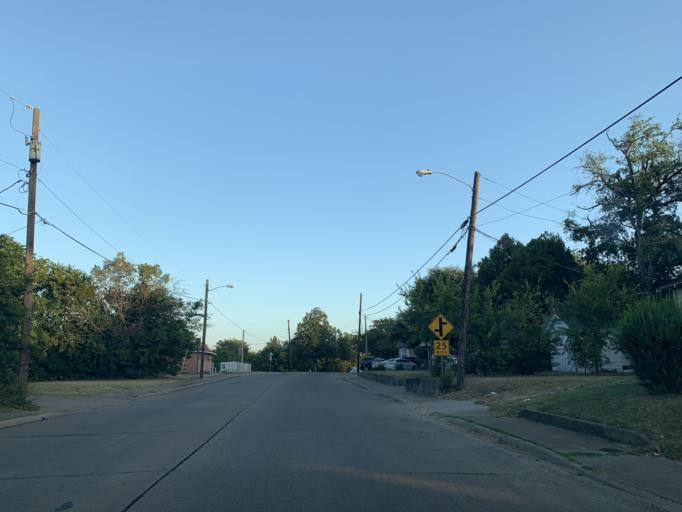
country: US
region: Texas
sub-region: Dallas County
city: Dallas
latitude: 32.6980
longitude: -96.8041
